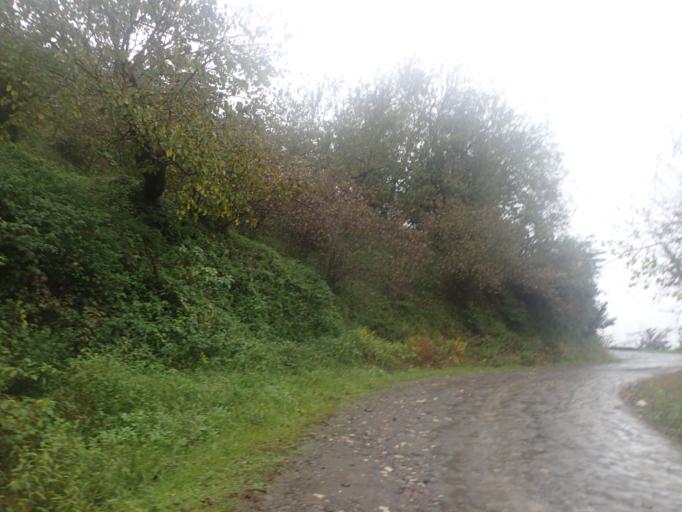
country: TR
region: Ordu
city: Persembe
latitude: 41.0350
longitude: 37.7181
